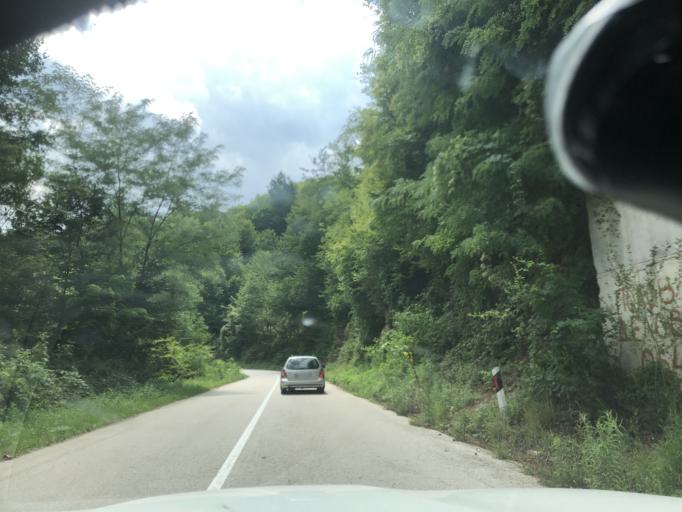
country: RS
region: Central Serbia
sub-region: Jablanicki Okrug
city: Medvega
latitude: 42.7929
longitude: 21.5814
